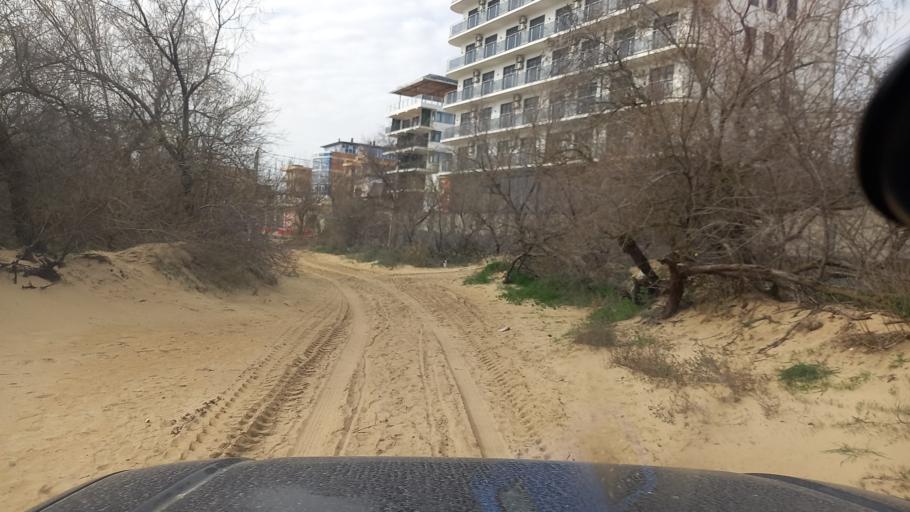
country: RU
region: Krasnodarskiy
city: Vityazevo
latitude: 44.9844
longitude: 37.2488
